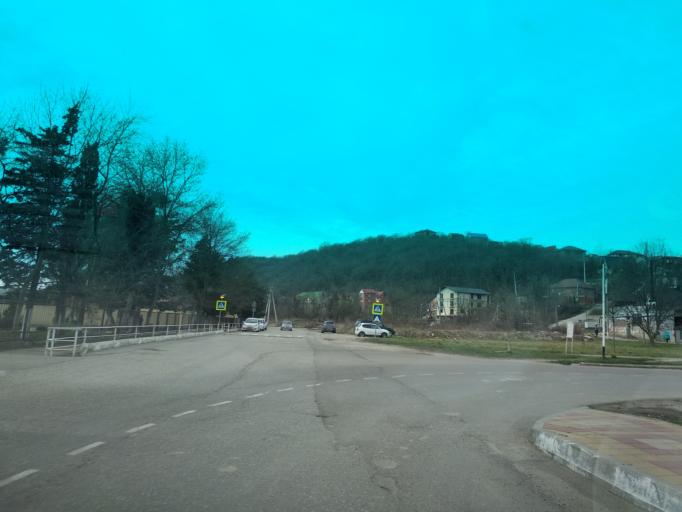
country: RU
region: Krasnodarskiy
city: Novomikhaylovskiy
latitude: 44.2491
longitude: 38.8394
